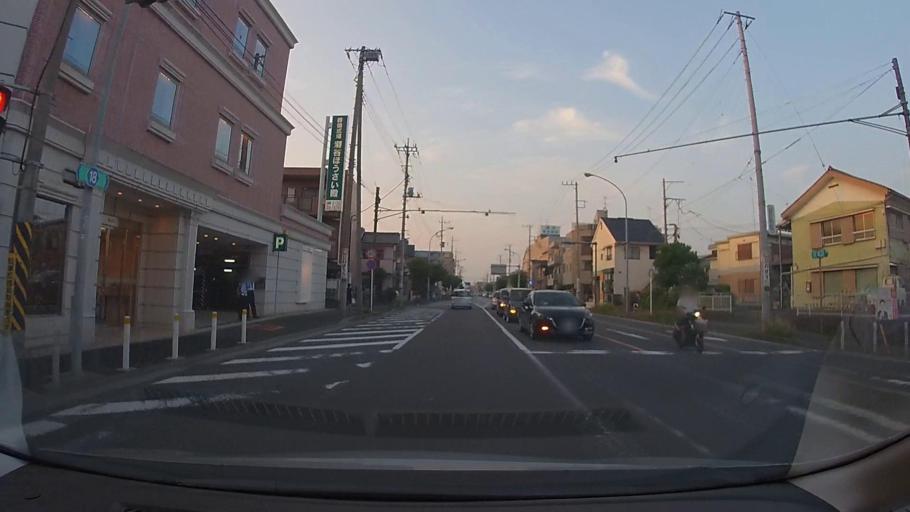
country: JP
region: Kanagawa
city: Minami-rinkan
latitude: 35.4652
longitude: 139.4799
